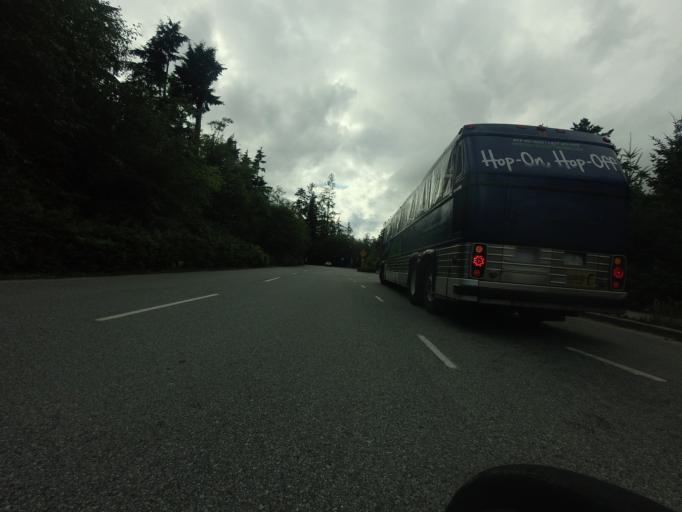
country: CA
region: British Columbia
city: West End
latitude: 49.3124
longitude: -123.1432
